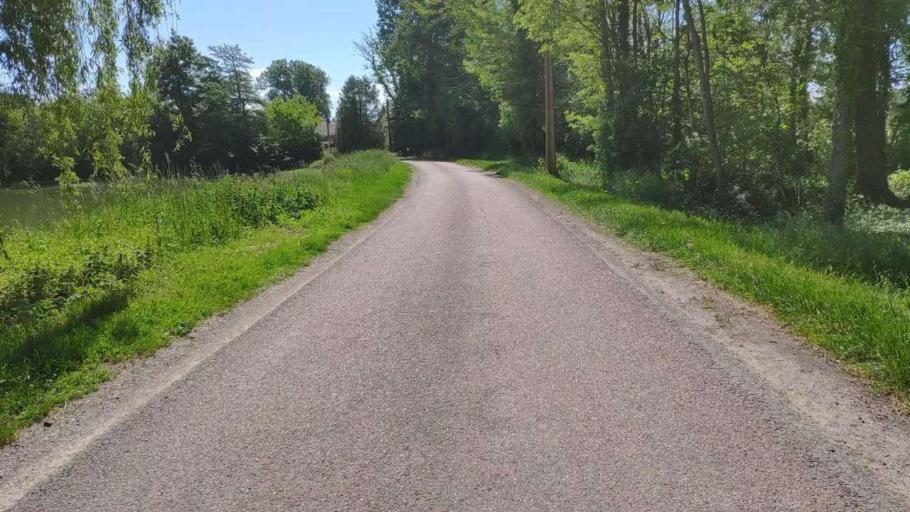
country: FR
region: Franche-Comte
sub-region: Departement du Jura
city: Bletterans
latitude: 46.7629
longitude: 5.4154
